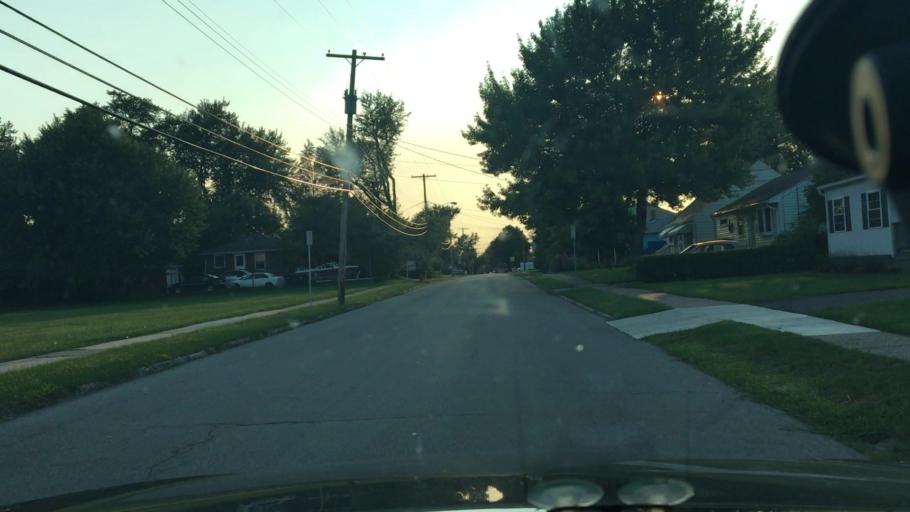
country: US
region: New York
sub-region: Erie County
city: Tonawanda
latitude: 43.0050
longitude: -78.8679
